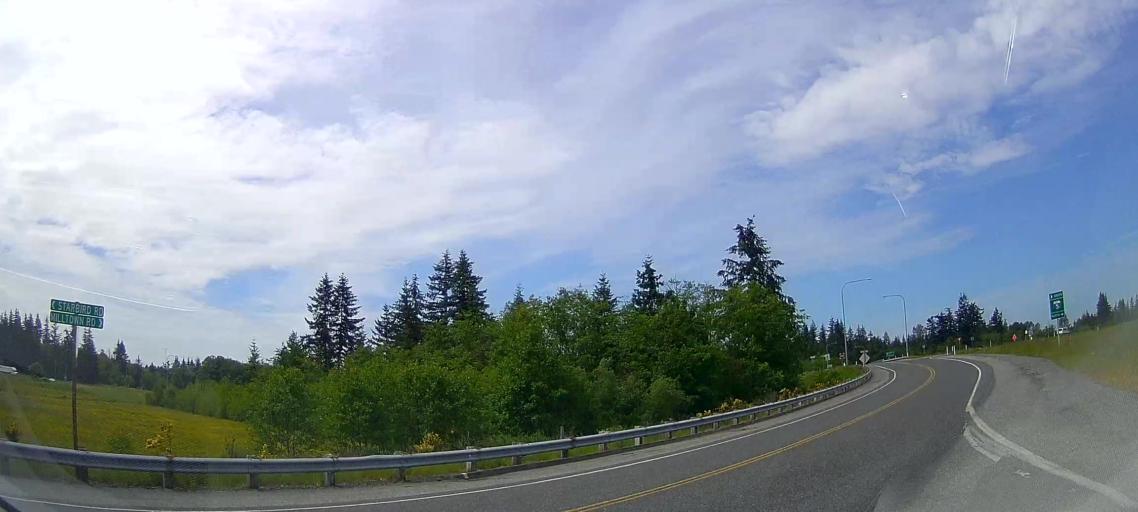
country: US
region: Washington
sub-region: Snohomish County
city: Stanwood
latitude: 48.3093
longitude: -122.3157
